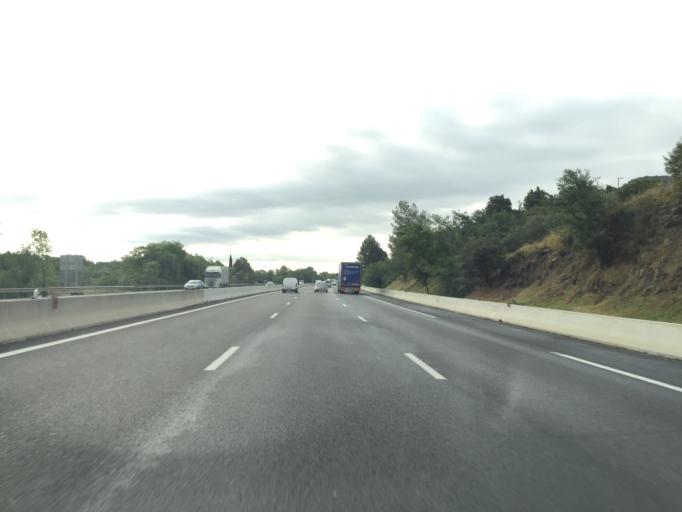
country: FR
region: Provence-Alpes-Cote d'Azur
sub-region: Departement du Var
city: Le Muy
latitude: 43.4642
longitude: 6.5759
